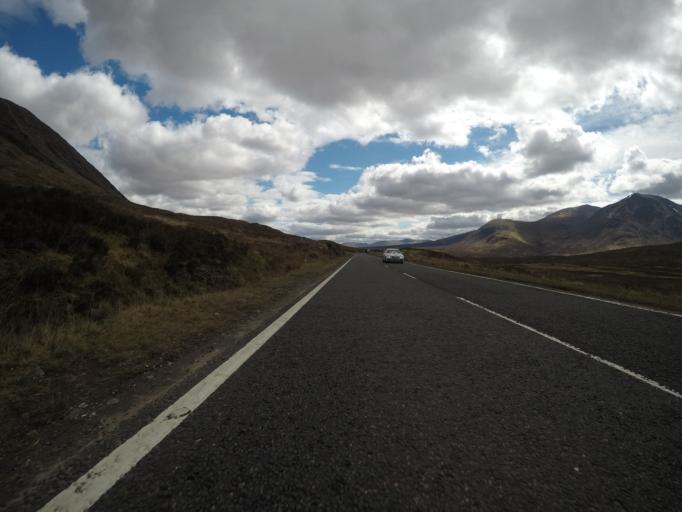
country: GB
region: Scotland
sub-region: Highland
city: Spean Bridge
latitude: 56.6592
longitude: -4.8837
